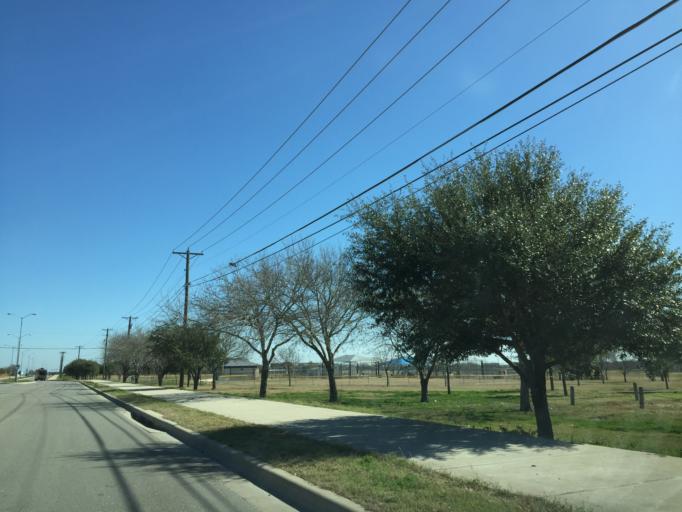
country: US
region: Texas
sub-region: Williamson County
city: Round Rock
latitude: 30.5463
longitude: -97.6238
